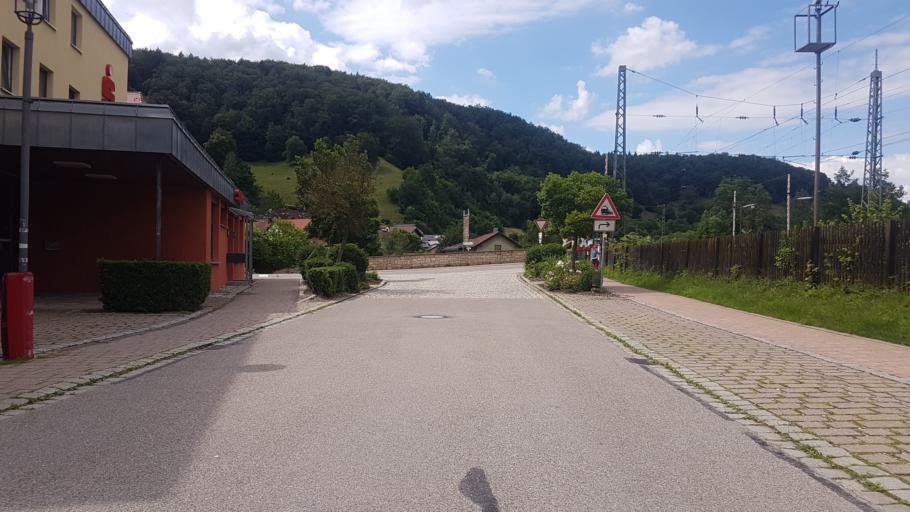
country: DE
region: Bavaria
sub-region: Regierungsbezirk Mittelfranken
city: Solnhofen
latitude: 48.8934
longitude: 10.9916
